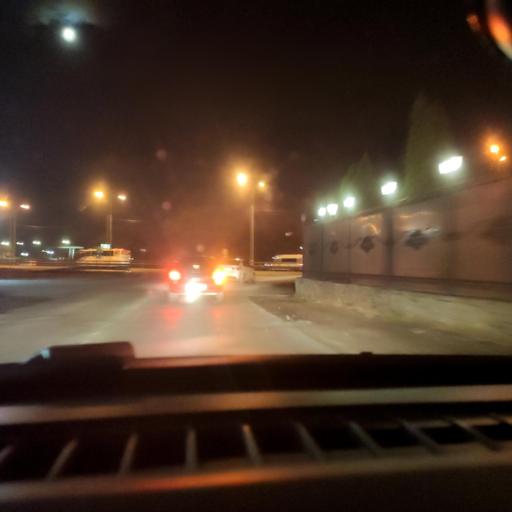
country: RU
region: Voronezj
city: Novaya Usman'
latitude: 51.6358
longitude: 39.3327
